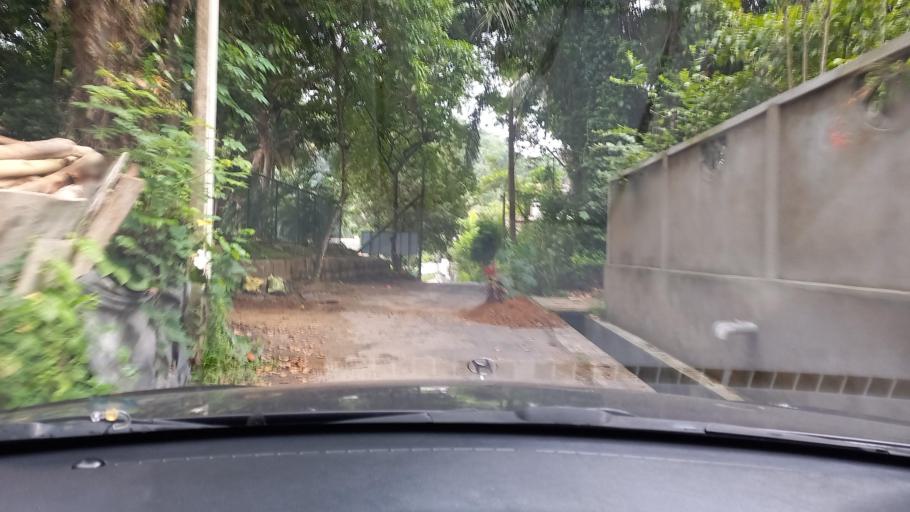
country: LK
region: Central
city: Kadugannawa
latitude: 7.2595
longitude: 80.3564
